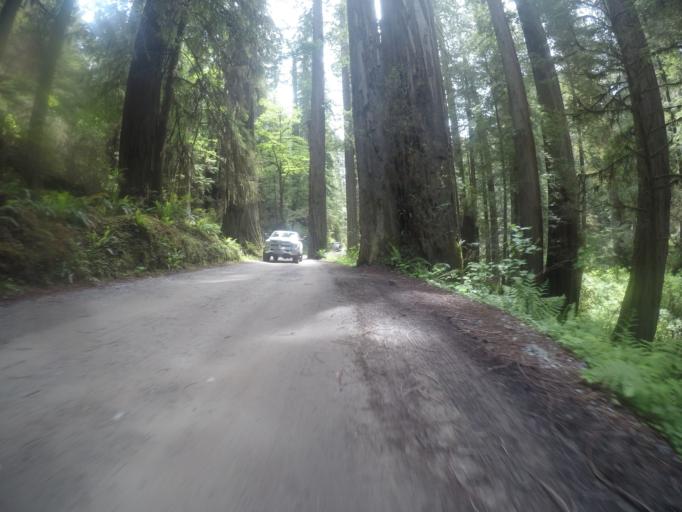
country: US
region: California
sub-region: Del Norte County
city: Bertsch-Oceanview
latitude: 41.7645
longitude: -124.1277
